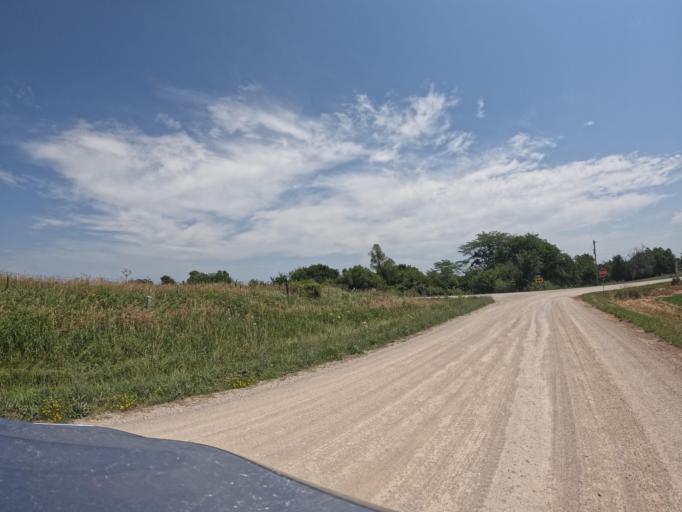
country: US
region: Iowa
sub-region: Appanoose County
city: Centerville
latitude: 40.7871
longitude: -92.9068
